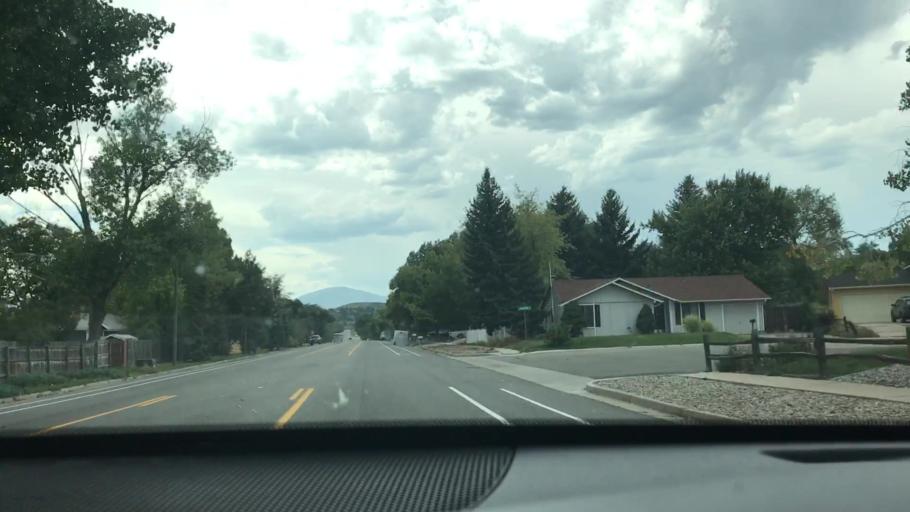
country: US
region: Colorado
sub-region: Larimer County
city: Loveland
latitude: 40.4147
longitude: -105.1133
